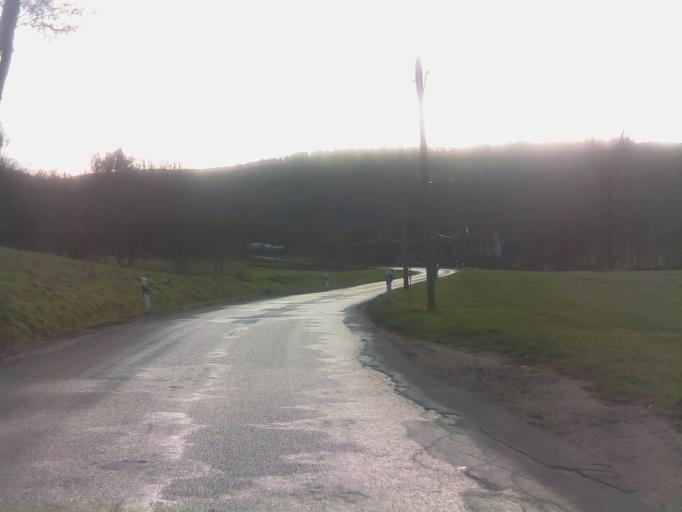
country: DE
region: Thuringia
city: Rottenbach
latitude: 50.7001
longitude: 11.2058
